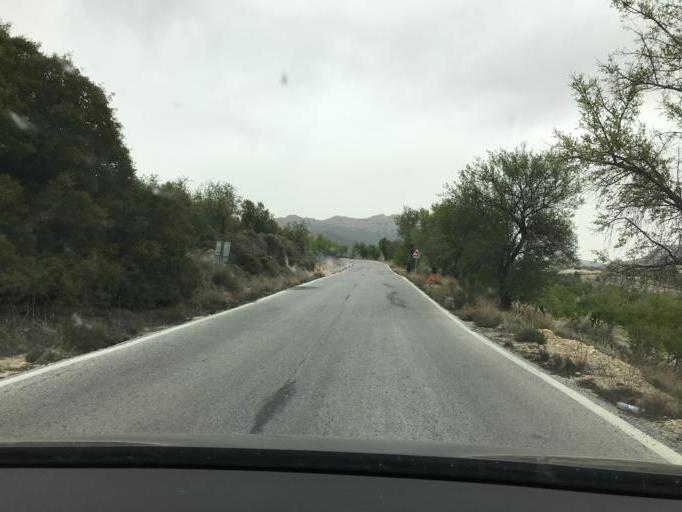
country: ES
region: Andalusia
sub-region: Provincia de Granada
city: Castril
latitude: 37.8061
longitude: -2.7646
